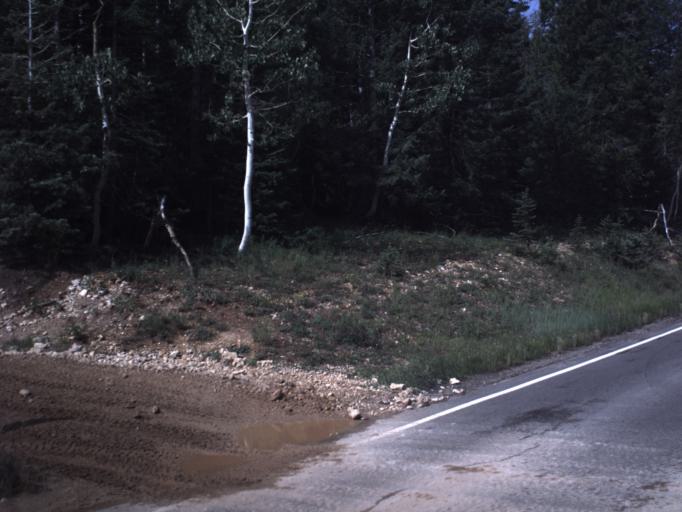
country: US
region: Utah
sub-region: Iron County
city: Parowan
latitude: 37.5151
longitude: -112.6939
